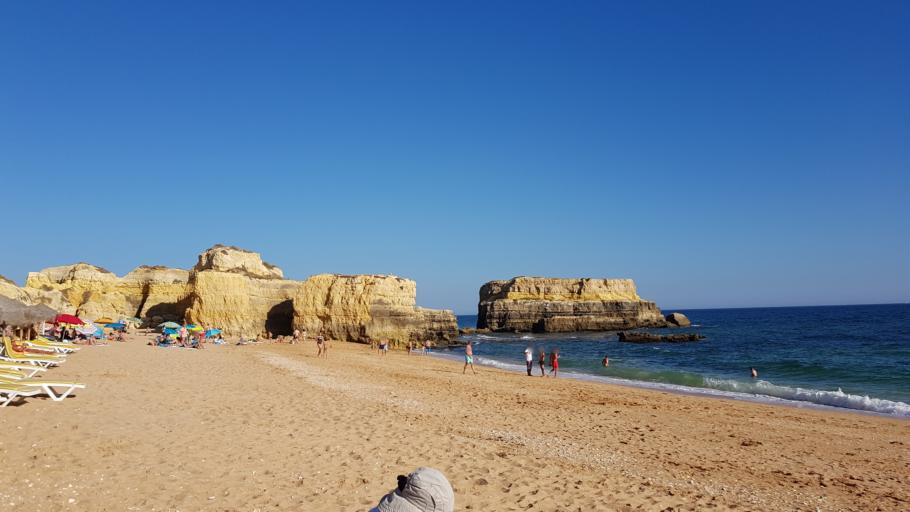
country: PT
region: Faro
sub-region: Albufeira
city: Albufeira
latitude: 37.0733
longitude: -8.2990
